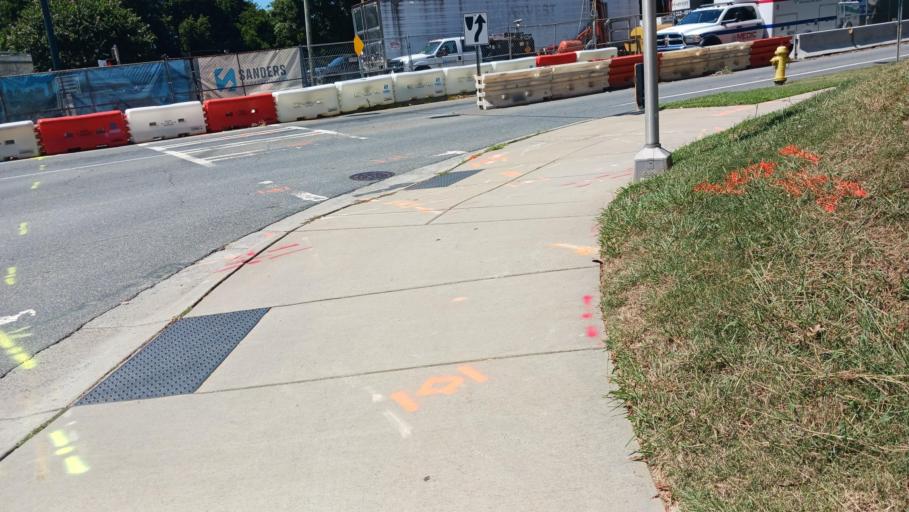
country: US
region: North Carolina
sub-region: Mecklenburg County
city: Charlotte
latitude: 35.2167
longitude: -80.8405
